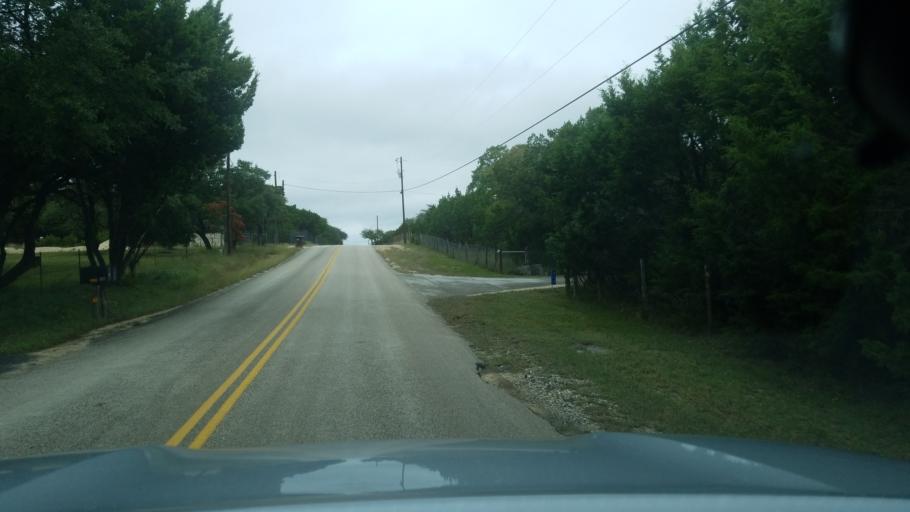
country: US
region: Texas
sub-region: Comal County
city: Bulverde
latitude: 29.7930
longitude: -98.4327
